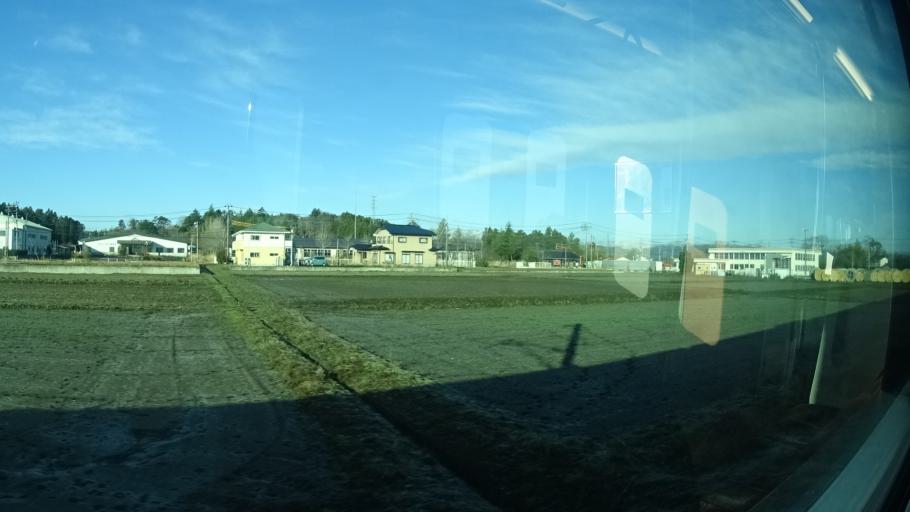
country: JP
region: Fukushima
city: Namie
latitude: 37.4833
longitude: 141.0013
